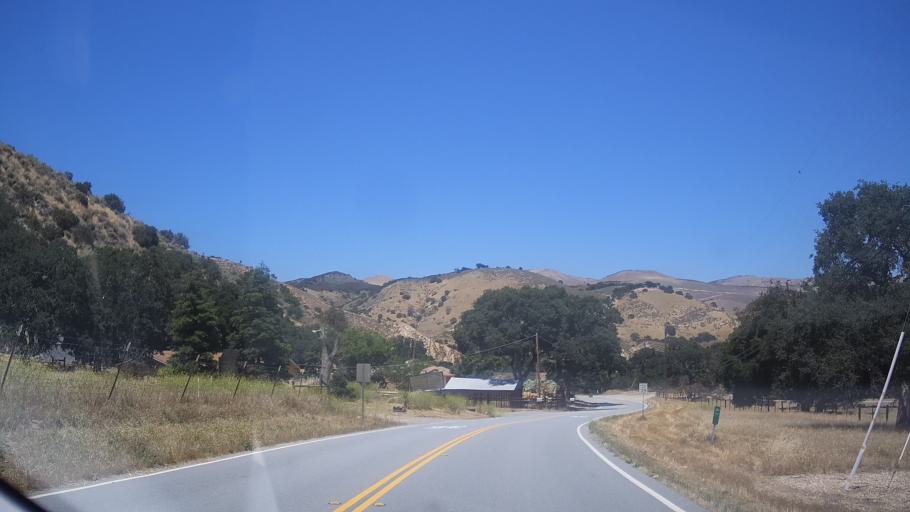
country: US
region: California
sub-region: Monterey County
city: Greenfield
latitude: 36.2498
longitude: -121.4320
